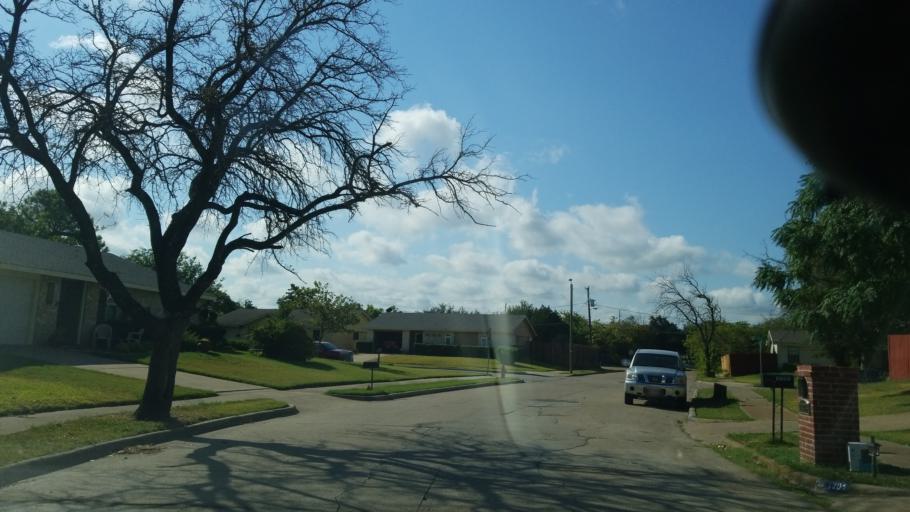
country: US
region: Texas
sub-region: Dallas County
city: Grand Prairie
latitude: 32.6947
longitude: -96.9991
